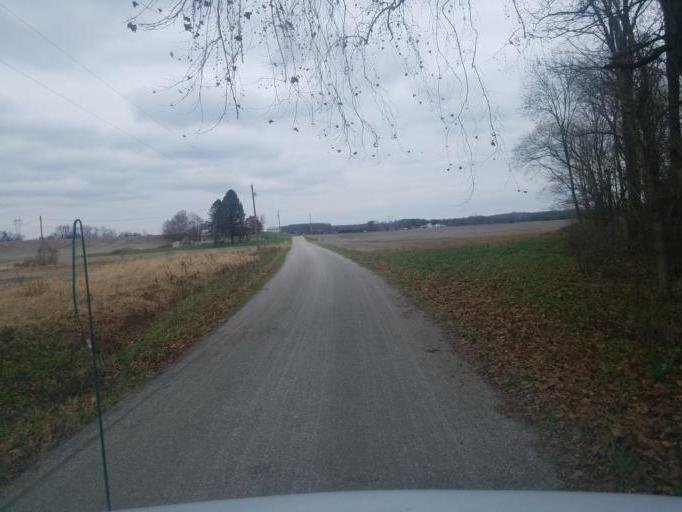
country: US
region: Ohio
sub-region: Knox County
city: Fredericktown
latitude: 40.5045
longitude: -82.5628
